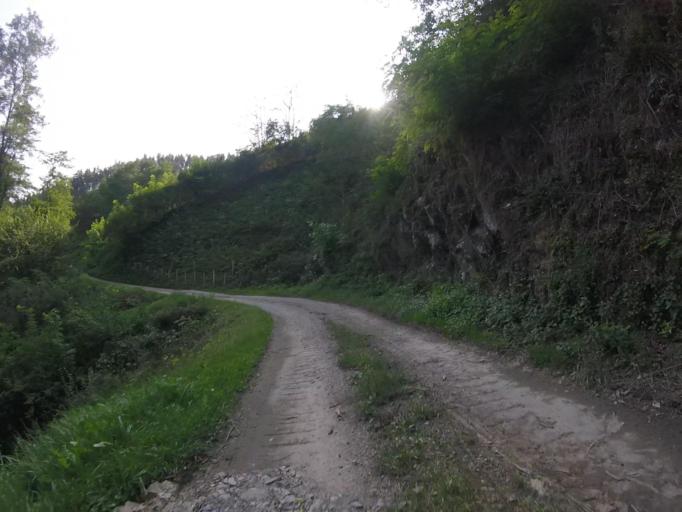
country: ES
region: Navarre
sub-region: Provincia de Navarra
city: Arano
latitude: 43.2320
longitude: -1.9348
